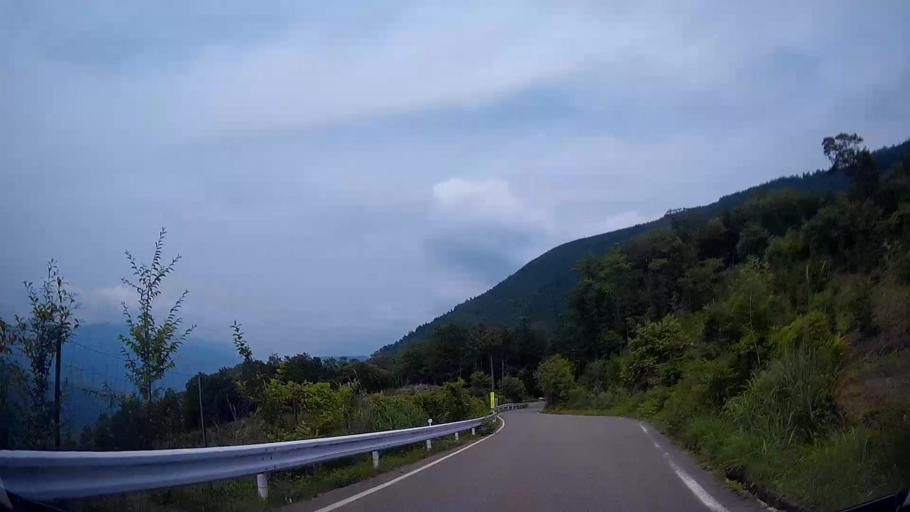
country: JP
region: Nagano
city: Iida
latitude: 35.2733
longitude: 137.9213
